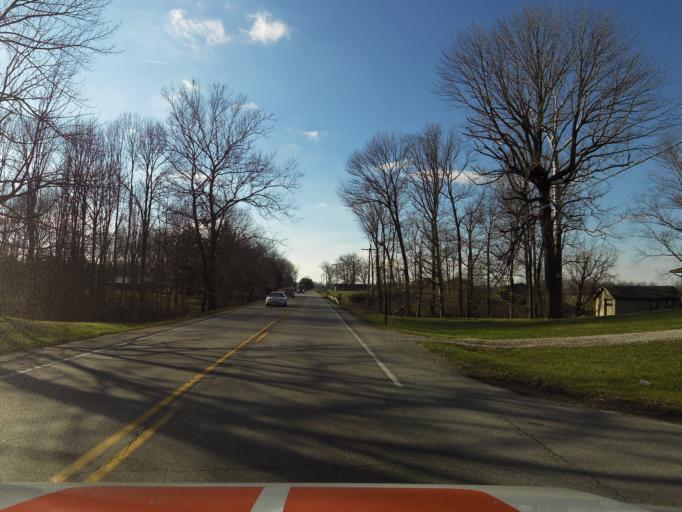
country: US
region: Indiana
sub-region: Jackson County
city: Seymour
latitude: 38.9668
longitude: -85.8064
